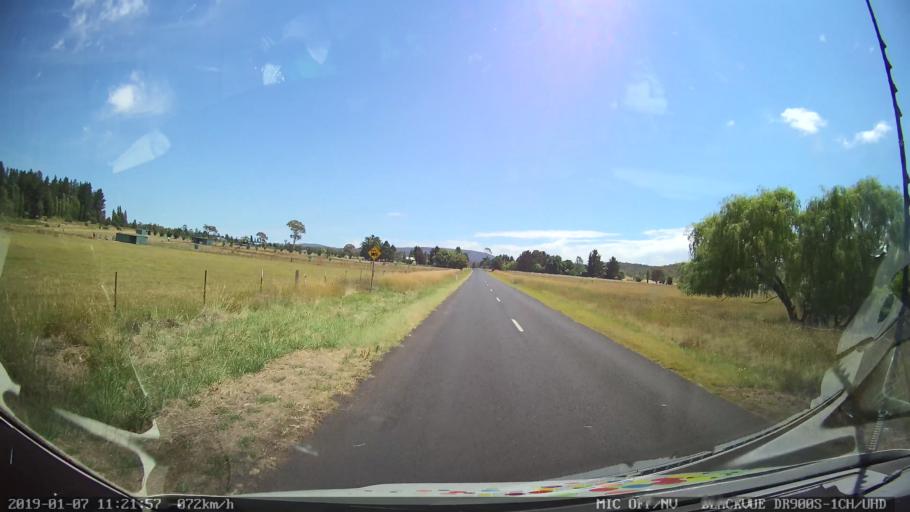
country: AU
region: New South Wales
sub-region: Armidale Dumaresq
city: Armidale
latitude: -30.4884
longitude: 151.6279
